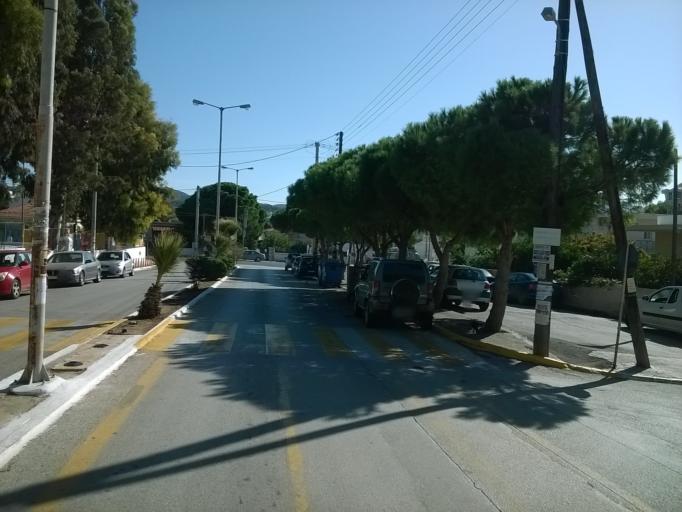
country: GR
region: Attica
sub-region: Nomarchia Anatolikis Attikis
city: Anavyssos
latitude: 37.7378
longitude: 23.9515
